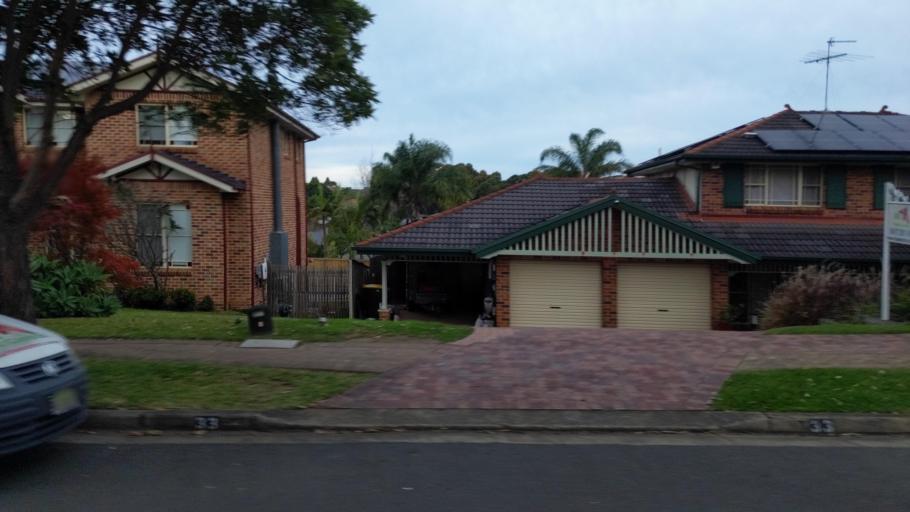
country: AU
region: New South Wales
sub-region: The Hills Shire
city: Baulkham Hills
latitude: -33.7415
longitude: 150.9603
